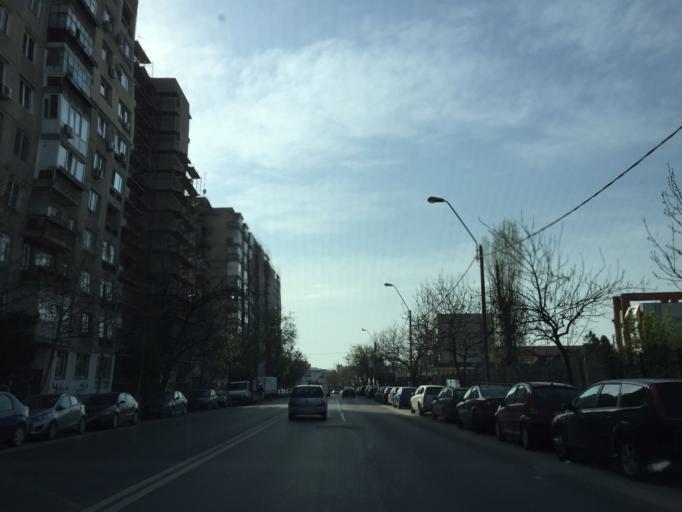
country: RO
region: Bucuresti
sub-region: Municipiul Bucuresti
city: Bucharest
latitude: 44.4107
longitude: 26.1364
